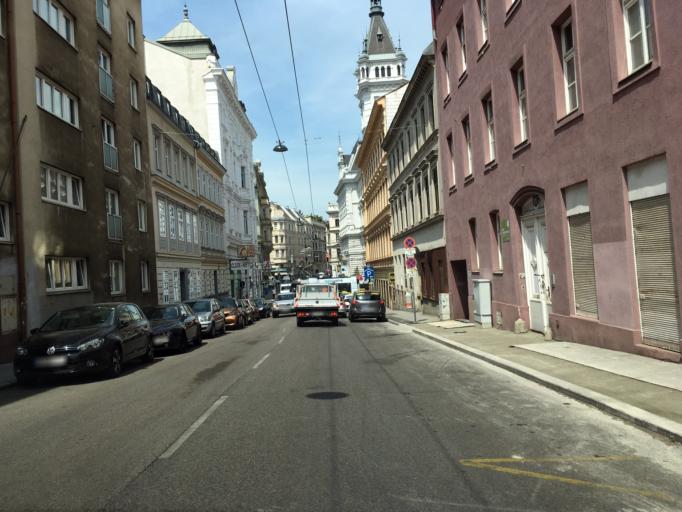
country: AT
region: Vienna
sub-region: Wien Stadt
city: Vienna
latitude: 48.2259
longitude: 16.3422
